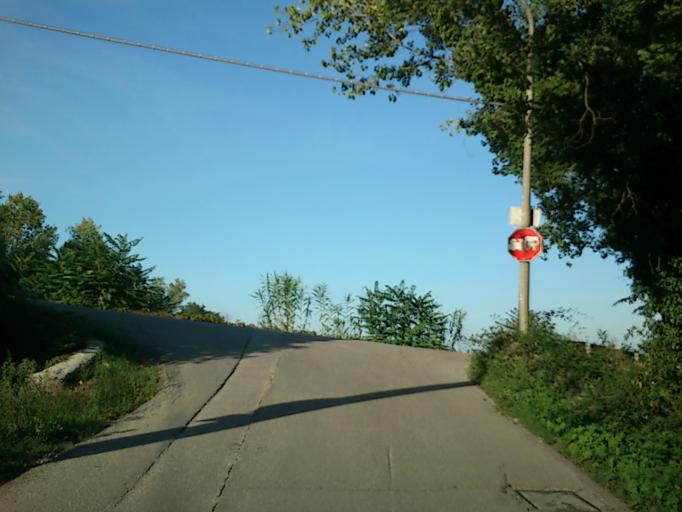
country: IT
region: The Marches
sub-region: Provincia di Pesaro e Urbino
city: Calcinelli
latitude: 43.7438
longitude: 12.9105
